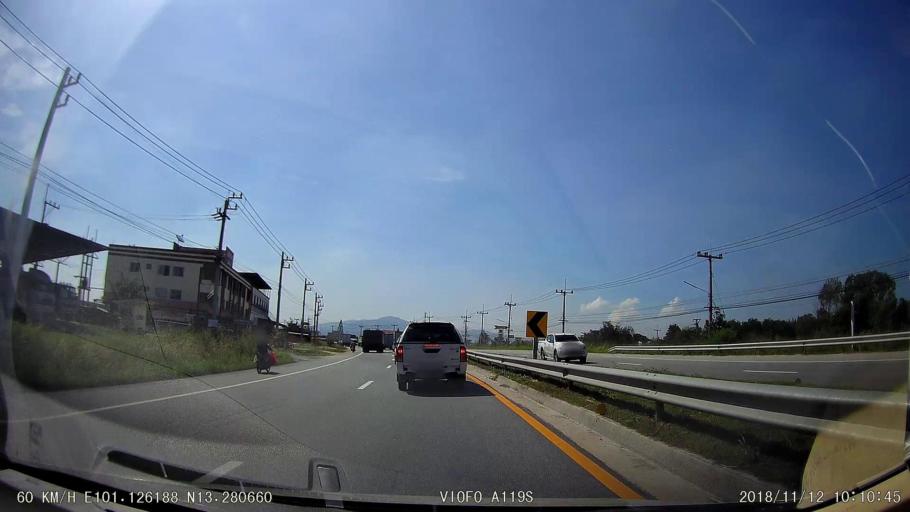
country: TH
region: Chon Buri
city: Ban Bueng
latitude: 13.2804
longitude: 101.1262
